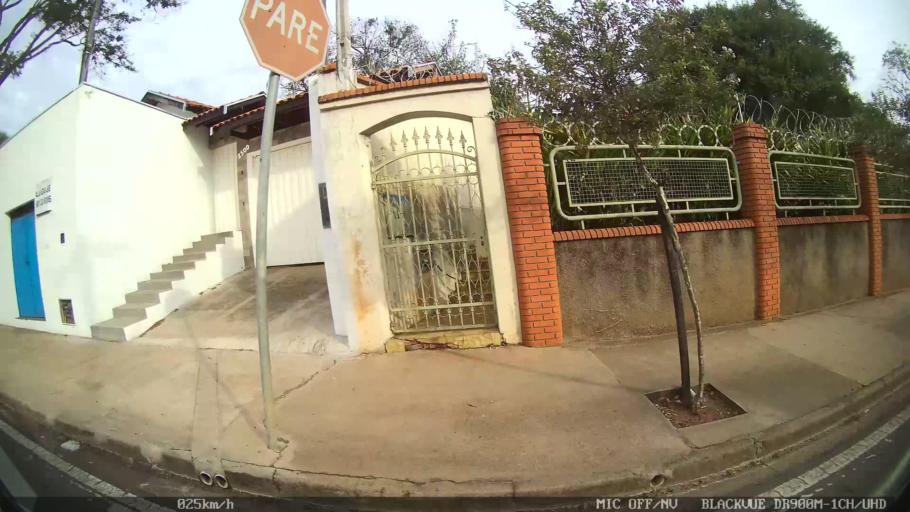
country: BR
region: Sao Paulo
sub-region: Piracicaba
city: Piracicaba
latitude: -22.7412
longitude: -47.6092
